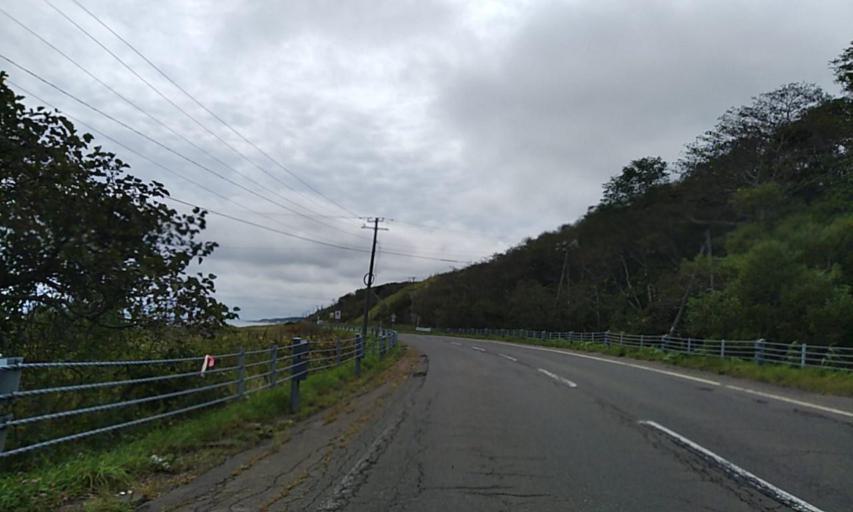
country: JP
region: Hokkaido
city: Shibetsu
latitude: 43.5075
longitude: 145.2451
